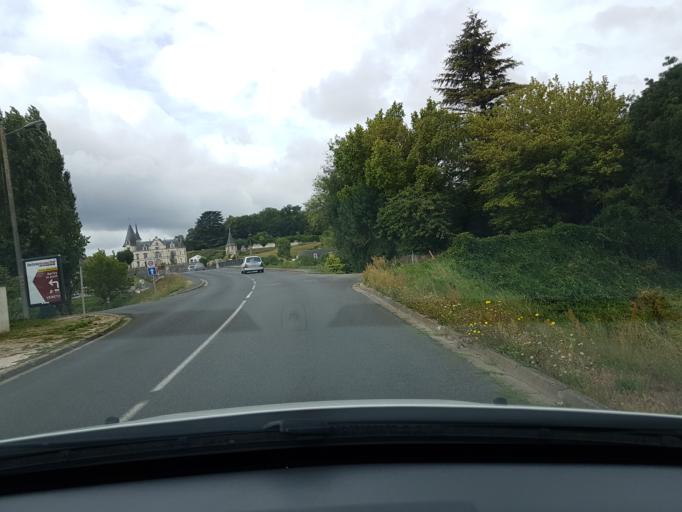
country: FR
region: Centre
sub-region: Departement d'Indre-et-Loire
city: Veretz
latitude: 47.3624
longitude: 0.8065
